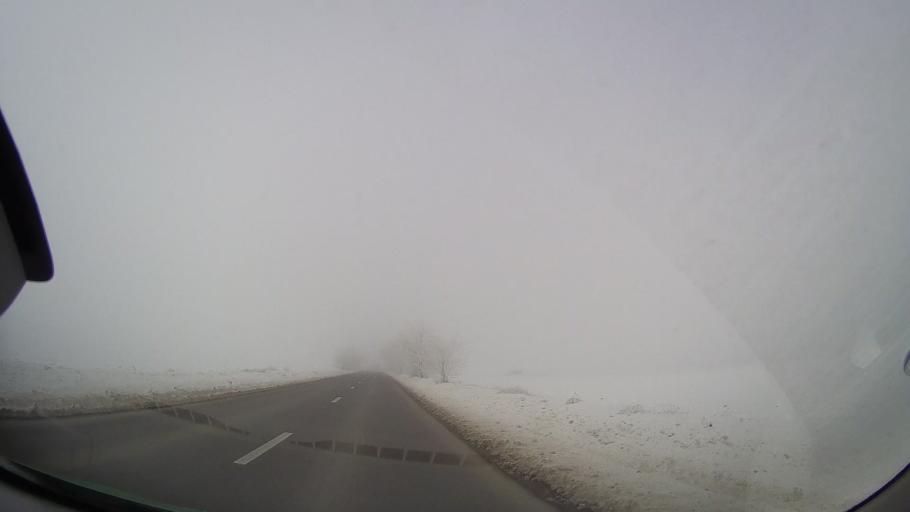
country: RO
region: Iasi
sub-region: Comuna Stolniceni-Prajescu
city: Stolniceni-Prajescu
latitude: 47.1859
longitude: 26.7400
